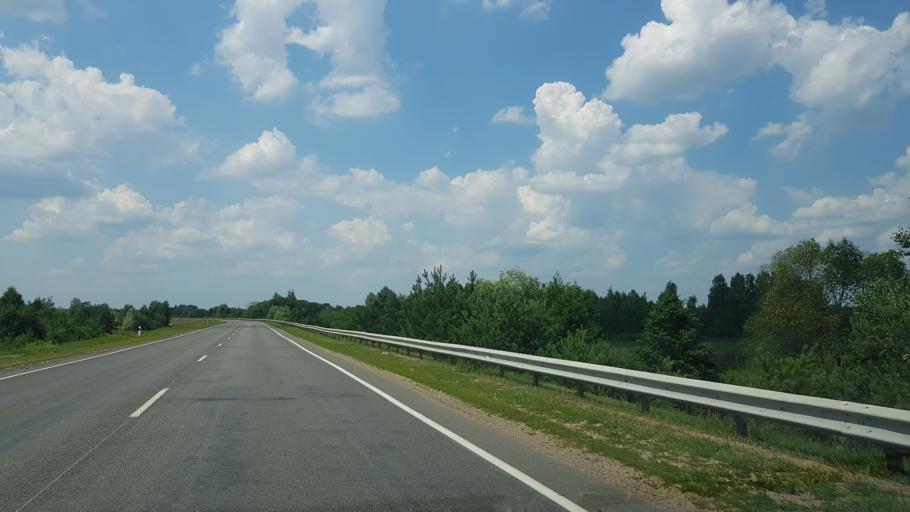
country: BY
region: Mogilev
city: Babruysk
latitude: 53.1669
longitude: 29.2804
